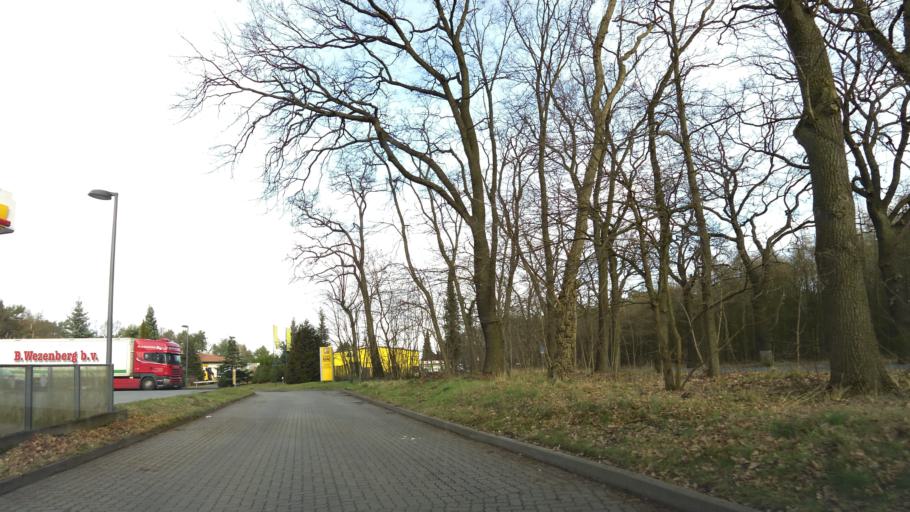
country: DE
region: Brandenburg
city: Michendorf
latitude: 52.3019
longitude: 13.0258
